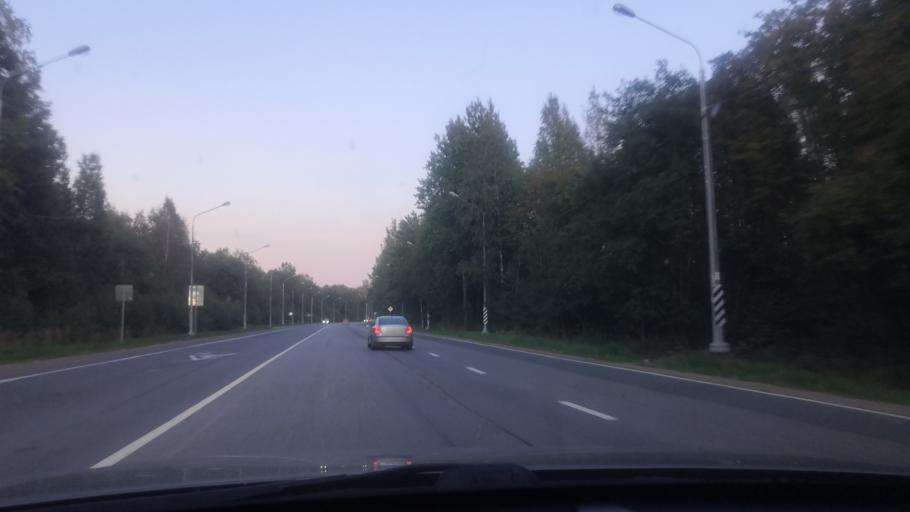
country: RU
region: St.-Petersburg
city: Beloostrov
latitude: 60.1958
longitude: 30.0593
